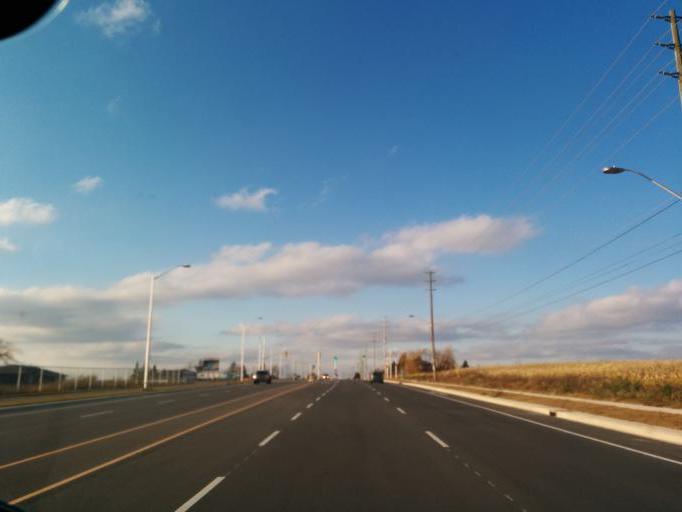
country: CA
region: Ontario
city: Oakville
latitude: 43.5048
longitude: -79.6930
